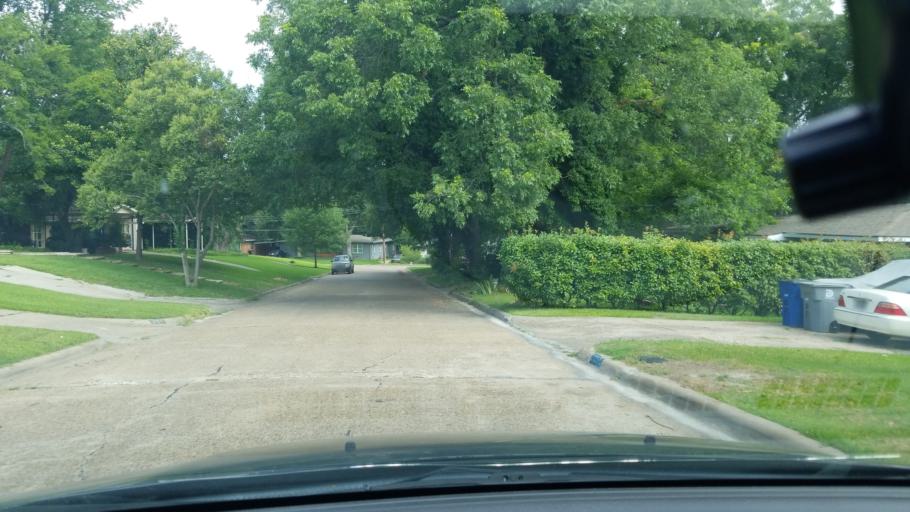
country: US
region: Texas
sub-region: Dallas County
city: Highland Park
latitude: 32.8108
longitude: -96.7057
